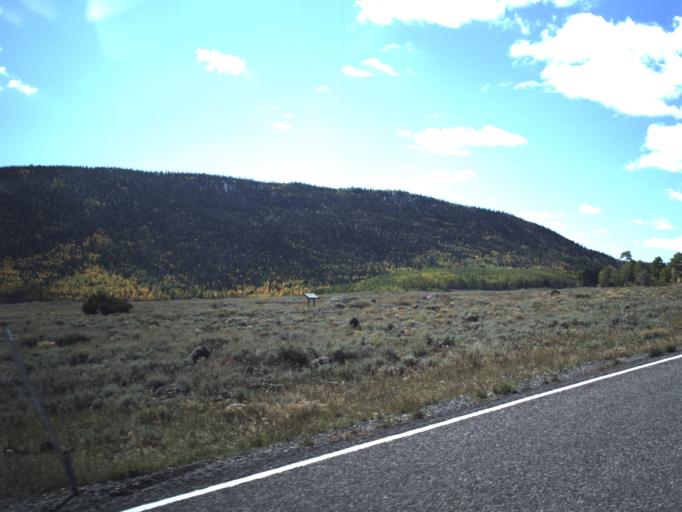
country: US
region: Utah
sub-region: Wayne County
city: Loa
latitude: 38.5327
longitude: -111.7388
